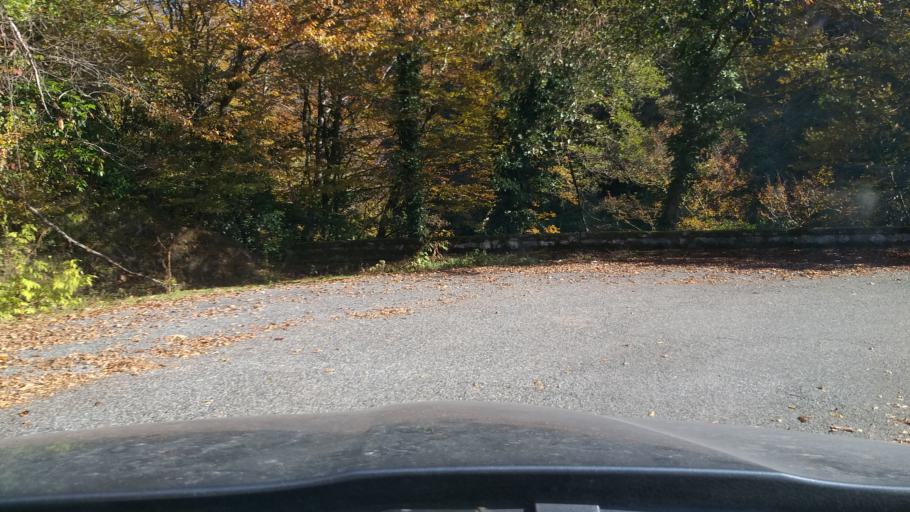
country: GE
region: Abkhazia
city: Bich'vinta
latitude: 43.1911
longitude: 40.4553
